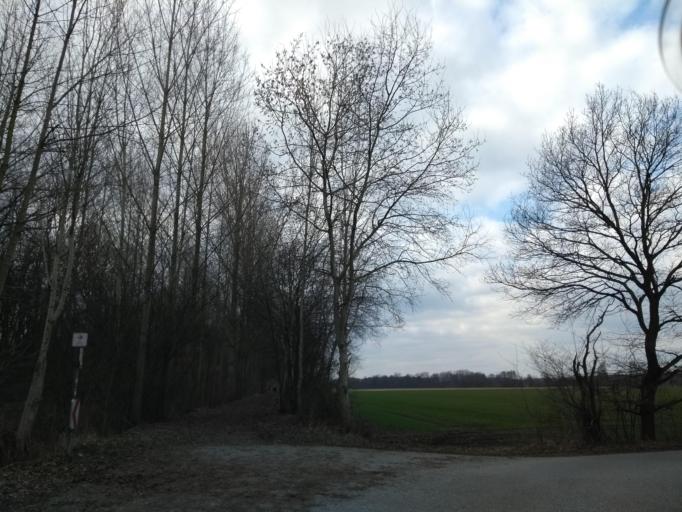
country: DE
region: North Rhine-Westphalia
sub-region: Regierungsbezirk Detmold
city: Delbruck
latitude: 51.7341
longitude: 8.4928
